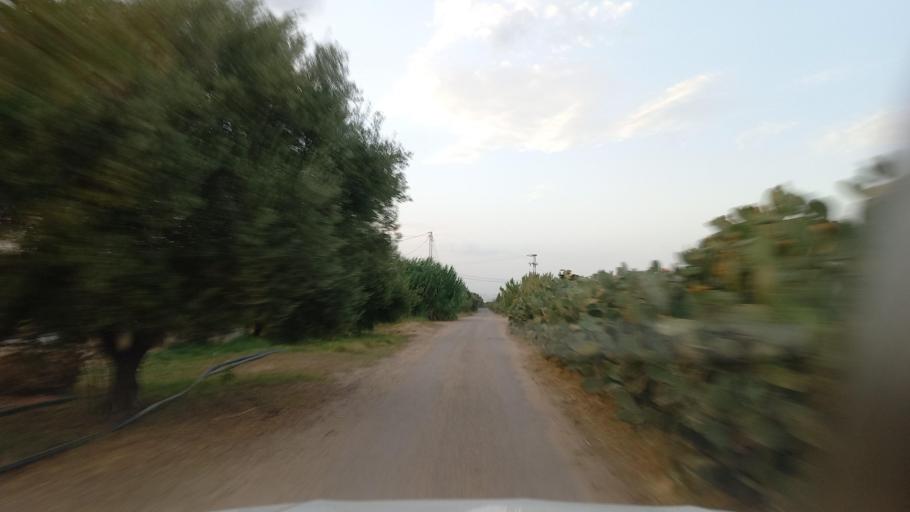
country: TN
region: Al Qasrayn
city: Kasserine
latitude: 35.2775
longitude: 9.0516
